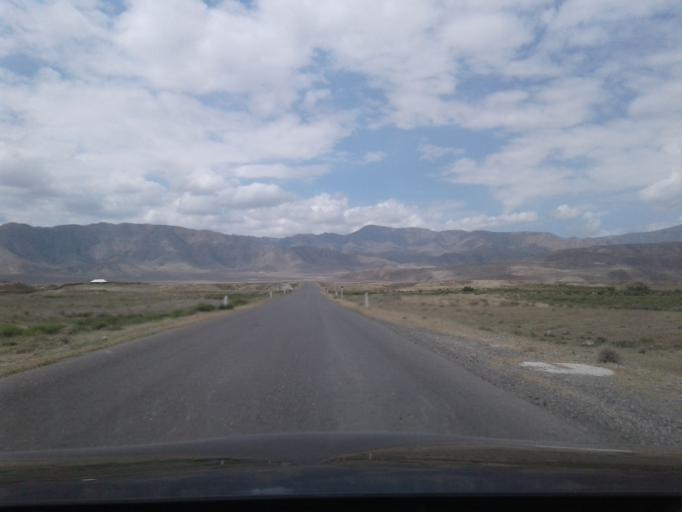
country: TM
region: Ahal
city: Baharly
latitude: 38.5317
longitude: 57.1500
